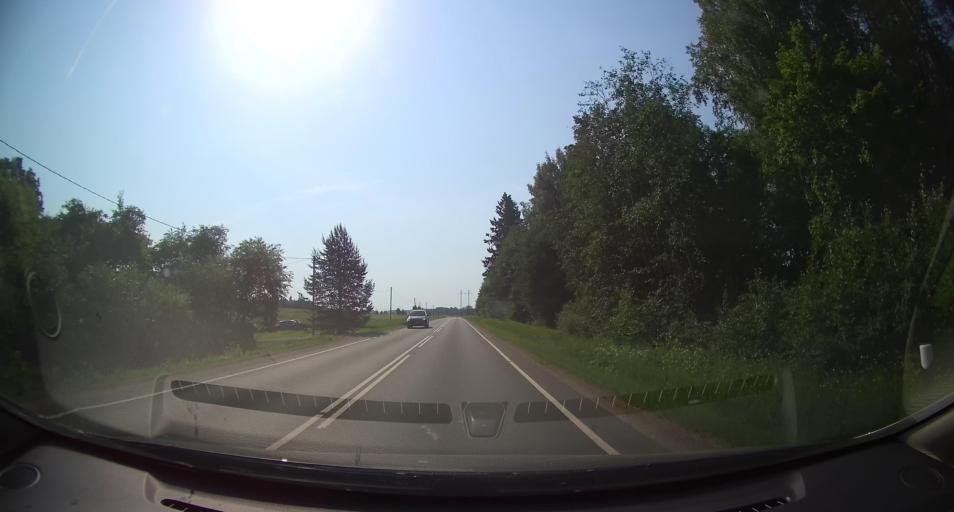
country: EE
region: Harju
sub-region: Anija vald
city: Kehra
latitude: 59.2587
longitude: 25.3172
